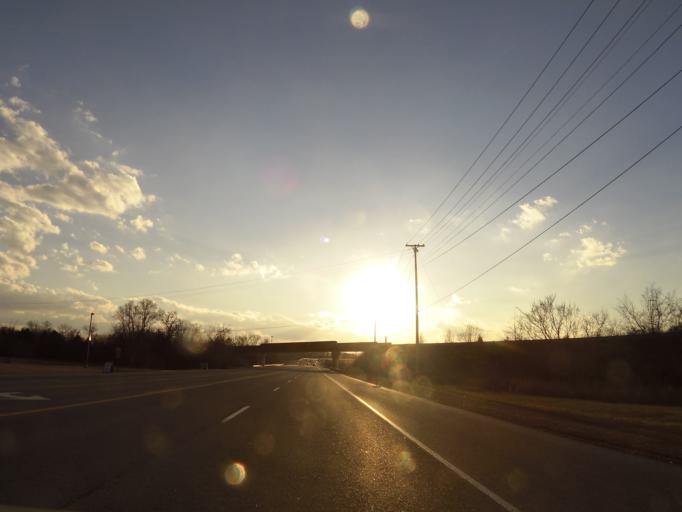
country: US
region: Tennessee
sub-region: Wilson County
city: Mount Juliet
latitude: 36.2357
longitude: -86.4194
